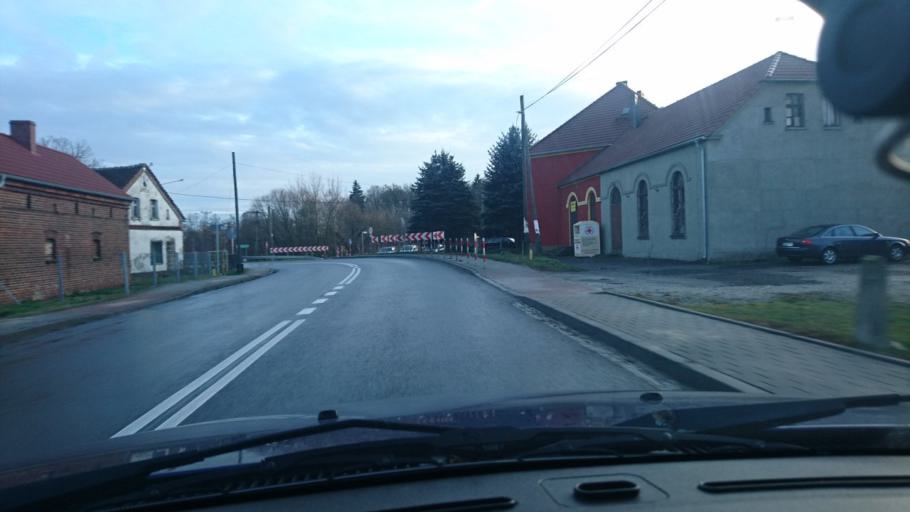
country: PL
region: Greater Poland Voivodeship
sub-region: Powiat kepinski
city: Opatow
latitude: 51.1658
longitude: 18.1476
